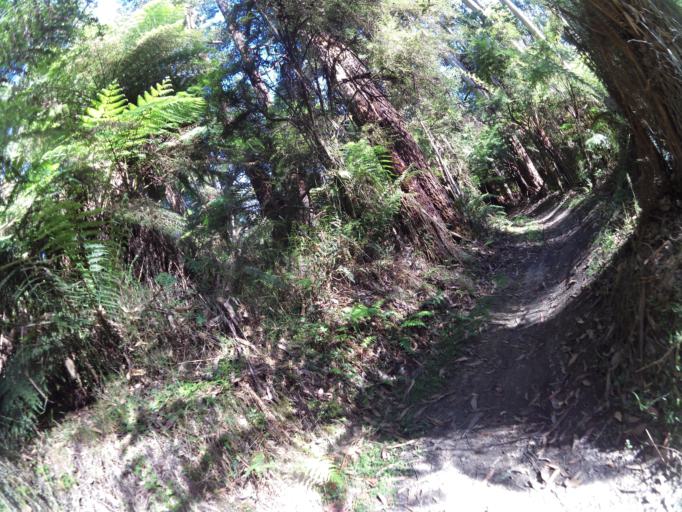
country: AU
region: Victoria
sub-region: Colac-Otway
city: Apollo Bay
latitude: -38.5504
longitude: 143.7445
